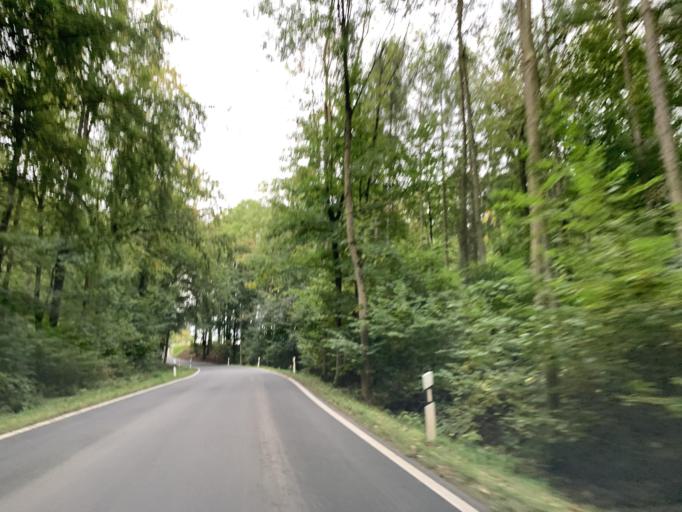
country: DE
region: Mecklenburg-Vorpommern
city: Burg Stargard
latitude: 53.4755
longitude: 13.2901
